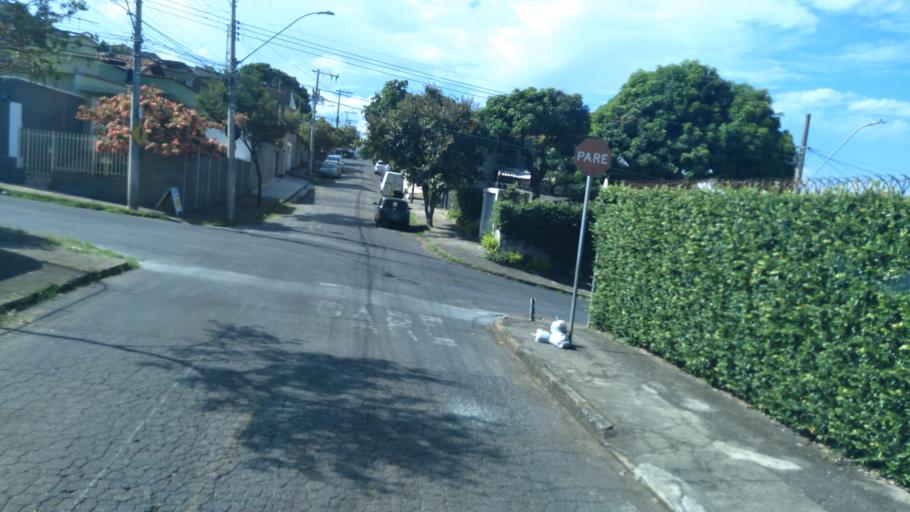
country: BR
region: Minas Gerais
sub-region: Belo Horizonte
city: Belo Horizonte
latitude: -19.8885
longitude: -43.8984
